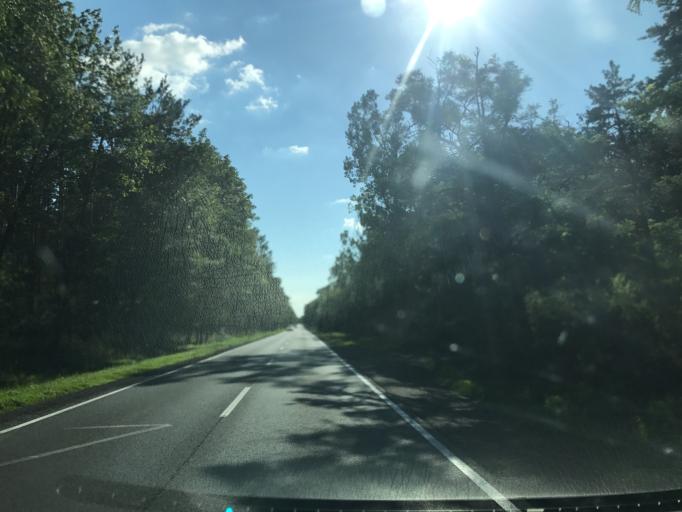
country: PL
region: Kujawsko-Pomorskie
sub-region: Wloclawek
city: Wloclawek
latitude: 52.6308
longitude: 19.0115
